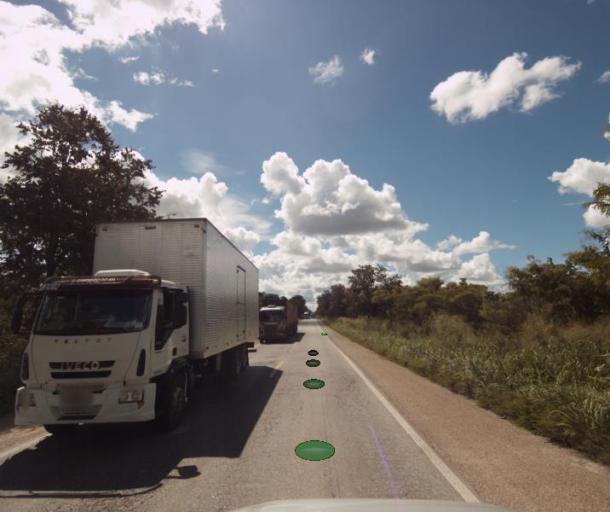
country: BR
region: Goias
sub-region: Porangatu
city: Porangatu
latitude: -13.6724
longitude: -49.0275
